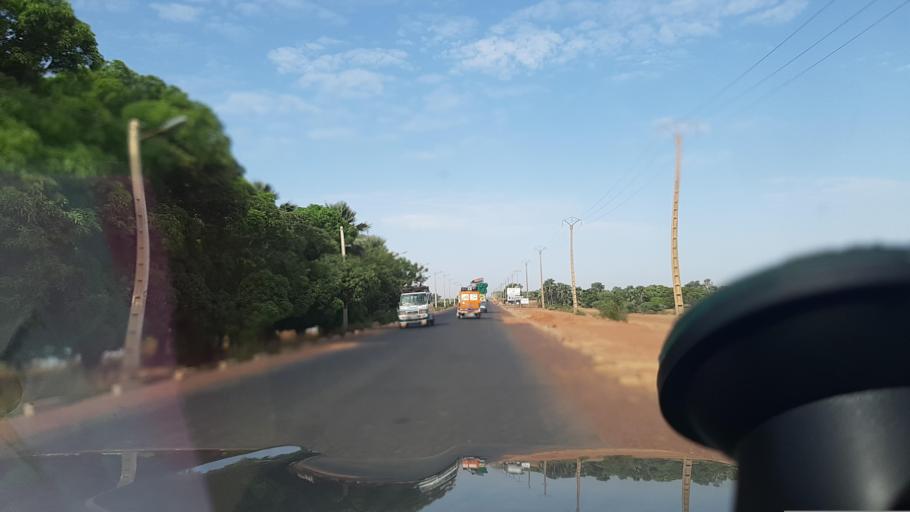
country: ML
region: Segou
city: Markala
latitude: 13.6822
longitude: -6.0873
